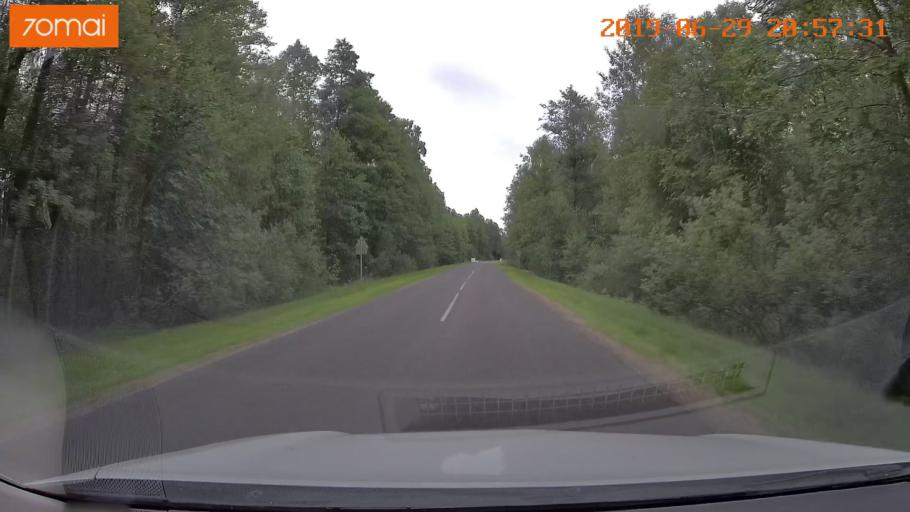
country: BY
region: Brest
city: Hantsavichy
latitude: 52.7201
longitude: 26.3715
